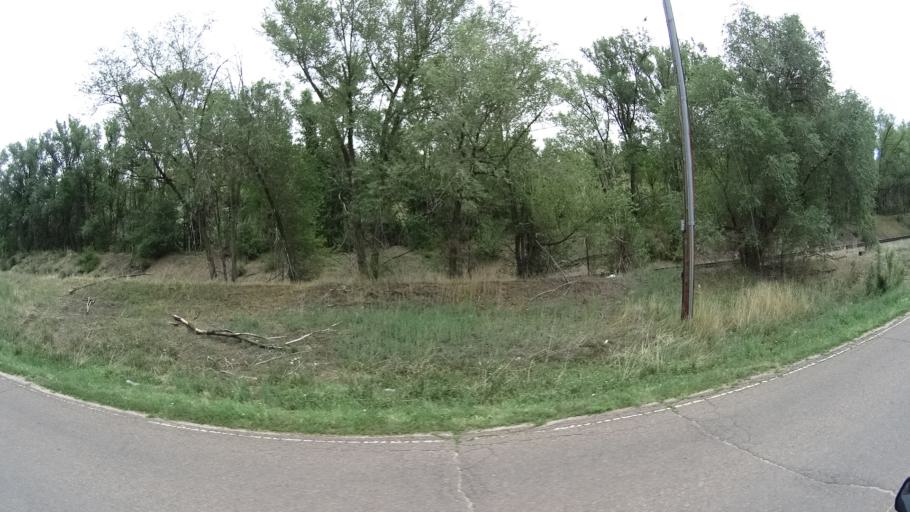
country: US
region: Colorado
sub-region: El Paso County
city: Fountain
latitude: 38.6921
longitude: -104.7024
